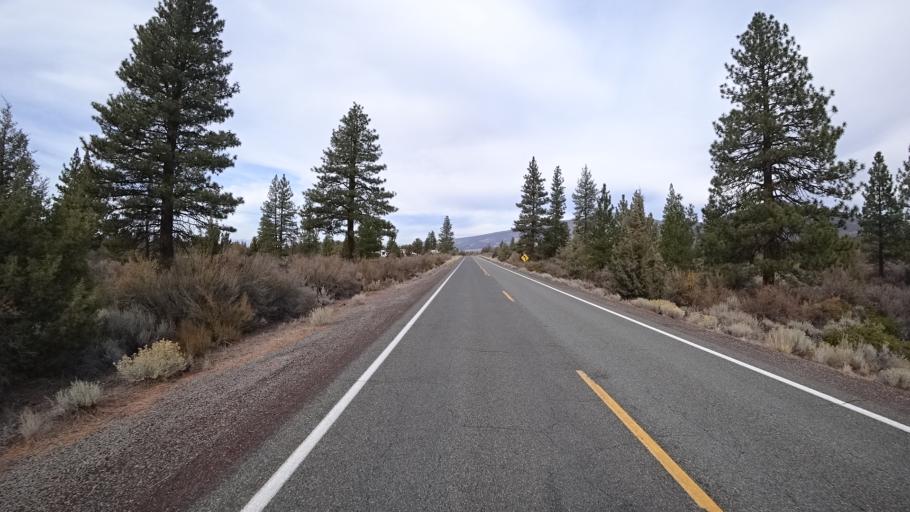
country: US
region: California
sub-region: Siskiyou County
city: Weed
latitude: 41.5477
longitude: -122.2481
